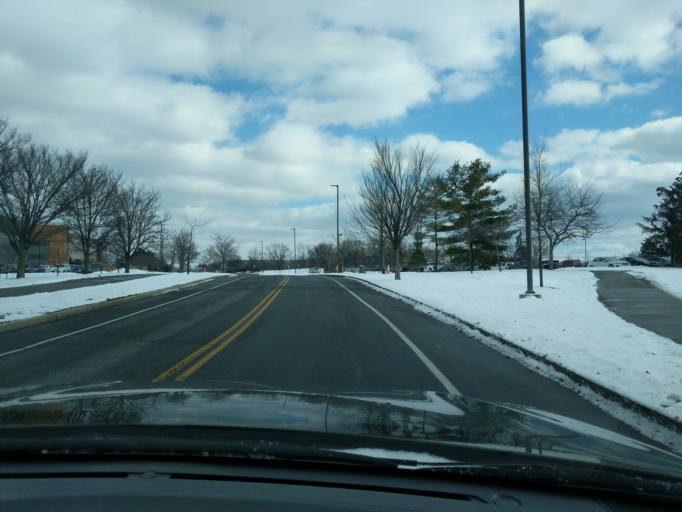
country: US
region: New York
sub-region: Tompkins County
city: East Ithaca
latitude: 42.4454
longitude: -76.4676
